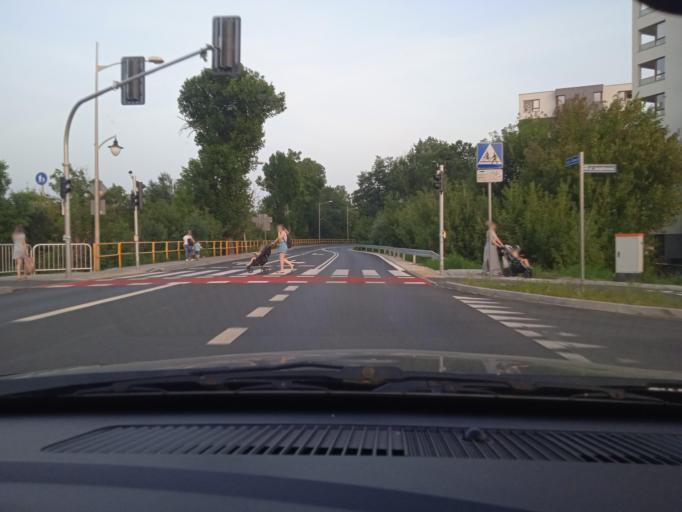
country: PL
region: Masovian Voivodeship
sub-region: Powiat nowodworski
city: Nowy Dwor Mazowiecki
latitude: 52.4216
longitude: 20.7278
